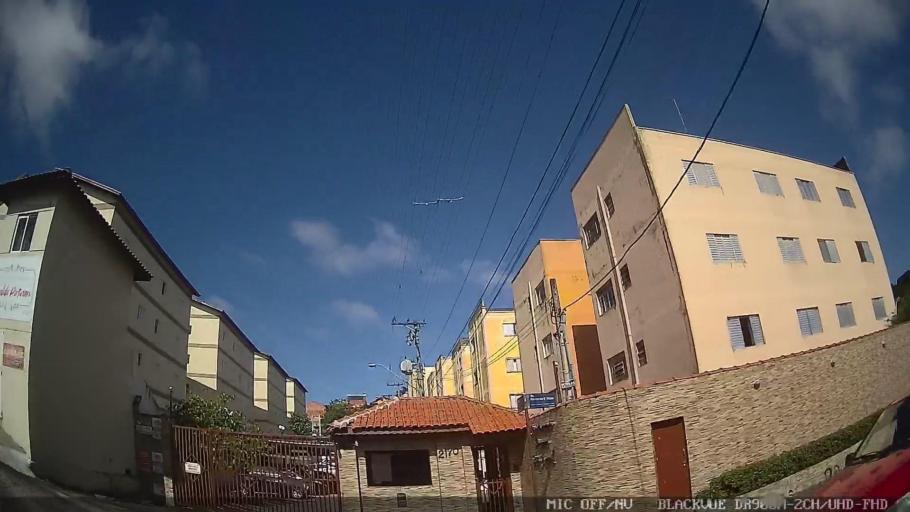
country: BR
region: Sao Paulo
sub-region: Itaquaquecetuba
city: Itaquaquecetuba
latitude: -23.4991
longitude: -46.3404
